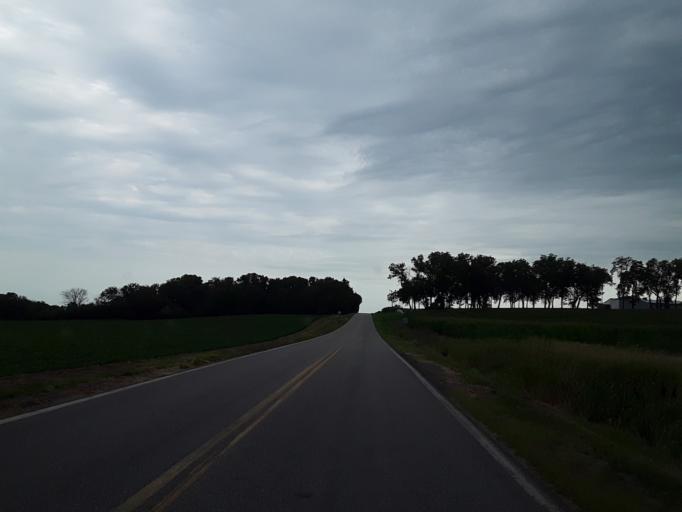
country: US
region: Nebraska
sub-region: Saunders County
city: Yutan
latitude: 41.2334
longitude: -96.3972
